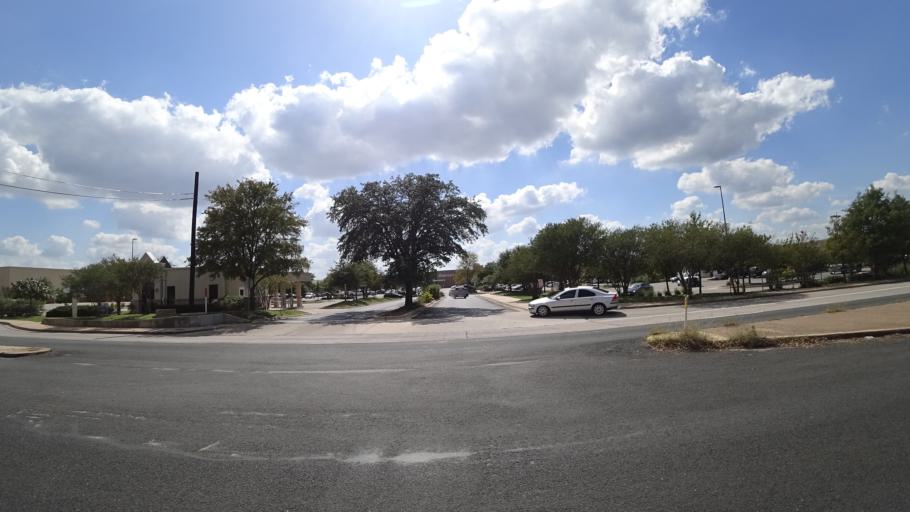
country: US
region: Texas
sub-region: Travis County
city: West Lake Hills
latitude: 30.3576
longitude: -97.7338
